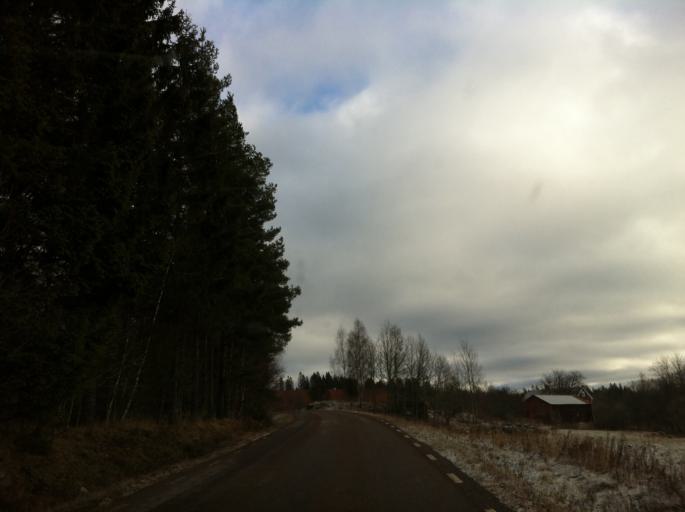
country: SE
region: Joenkoeping
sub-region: Eksjo Kommun
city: Mariannelund
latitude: 57.6105
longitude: 15.6959
